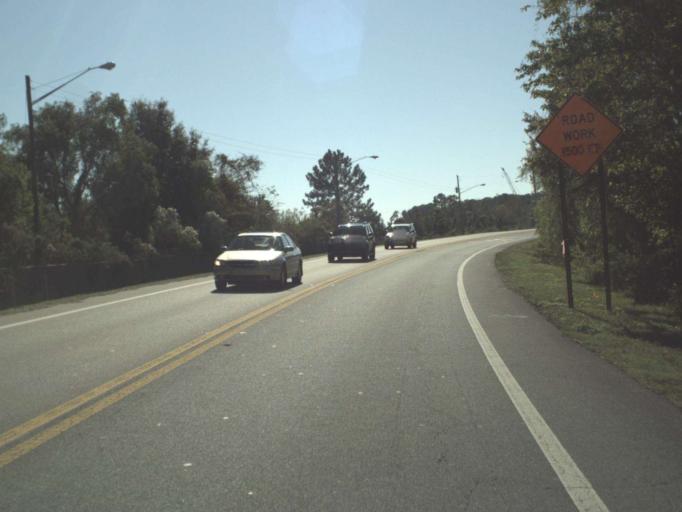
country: US
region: Florida
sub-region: Escambia County
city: Ferry Pass
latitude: 30.5154
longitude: -87.1650
